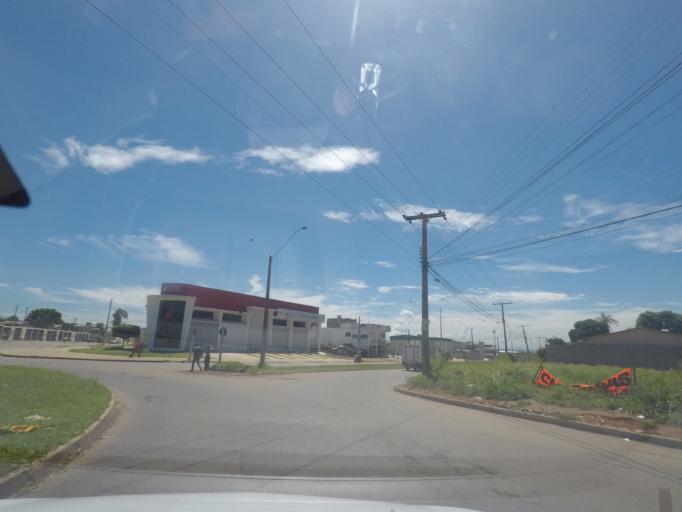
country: BR
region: Goias
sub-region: Aparecida De Goiania
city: Aparecida de Goiania
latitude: -16.7698
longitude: -49.3231
